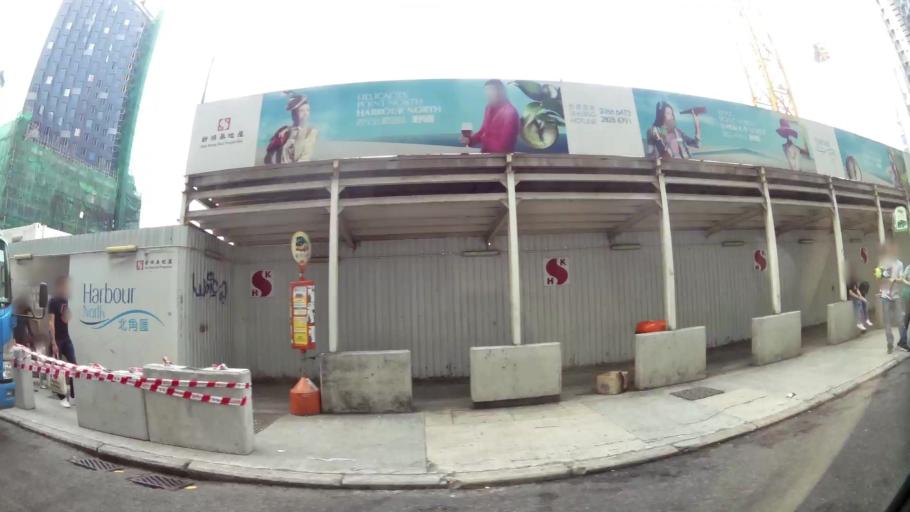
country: HK
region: Kowloon City
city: Kowloon
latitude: 22.2925
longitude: 114.2011
